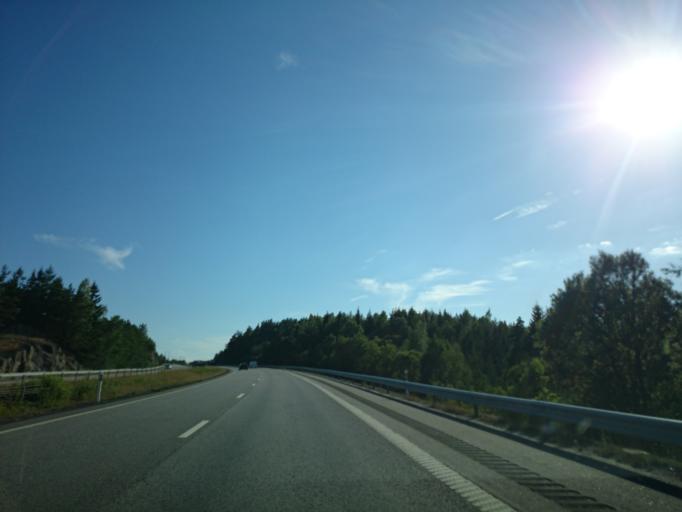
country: SE
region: Soedermanland
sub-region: Oxelosunds Kommun
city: Oxelosund
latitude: 58.8400
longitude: 17.1803
